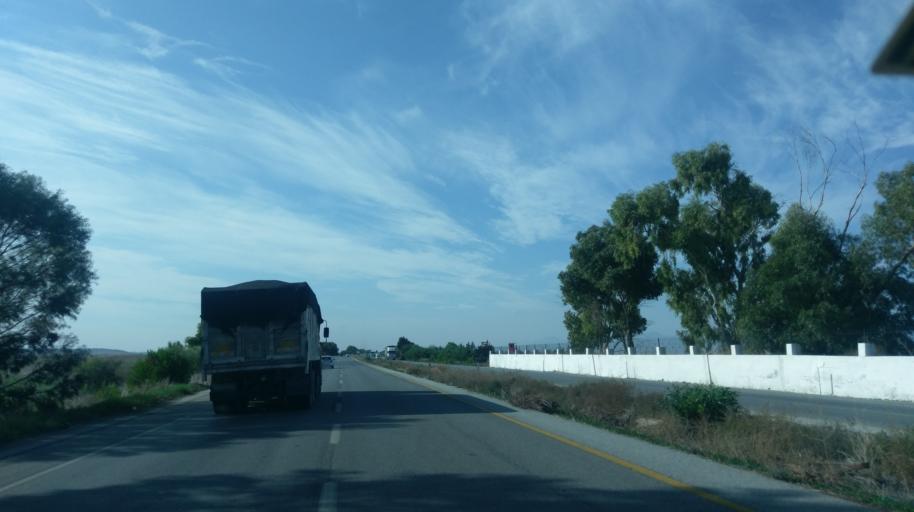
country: CY
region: Ammochostos
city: Lefkonoiko
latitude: 35.1801
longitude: 33.7250
